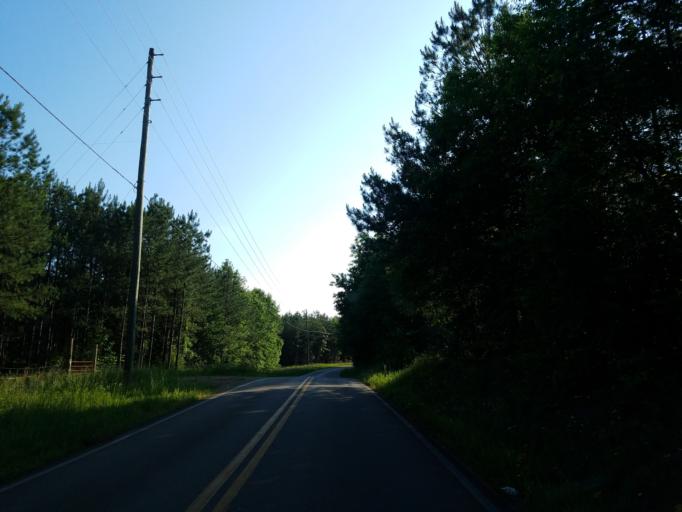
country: US
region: Georgia
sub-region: Pickens County
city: Nelson
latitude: 34.3858
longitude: -84.3194
